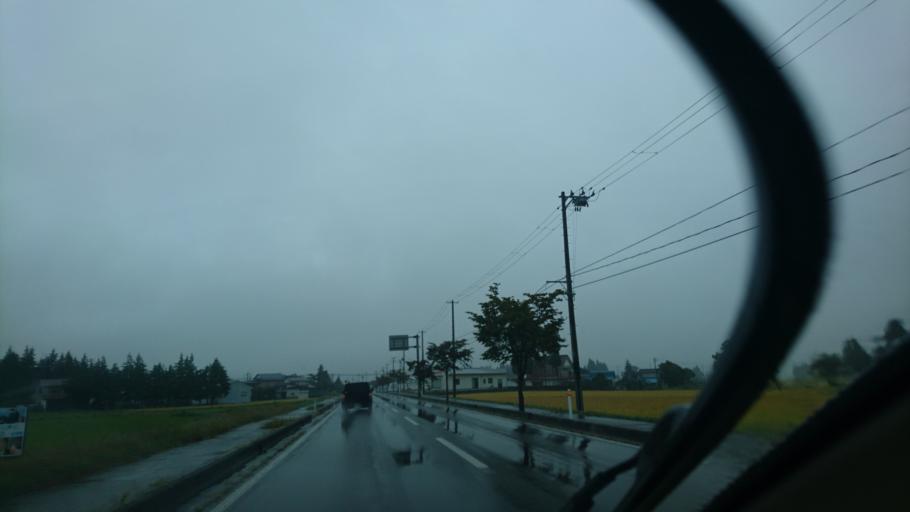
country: JP
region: Iwate
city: Mizusawa
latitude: 39.1319
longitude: 141.0655
